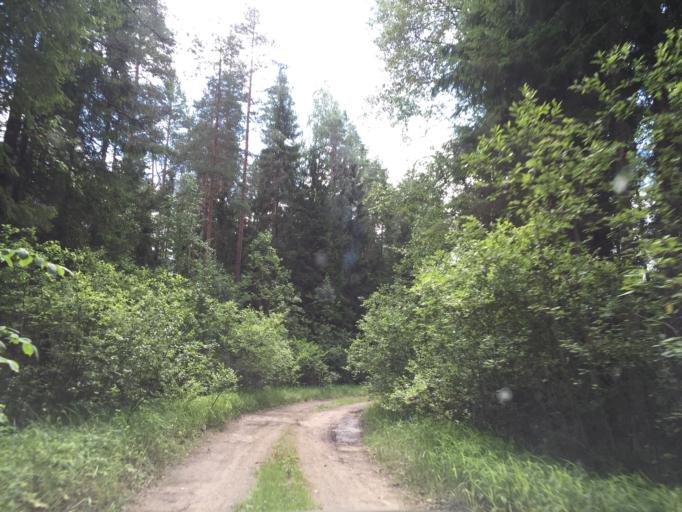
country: LV
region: Ropazu
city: Ropazi
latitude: 56.8986
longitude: 24.7157
